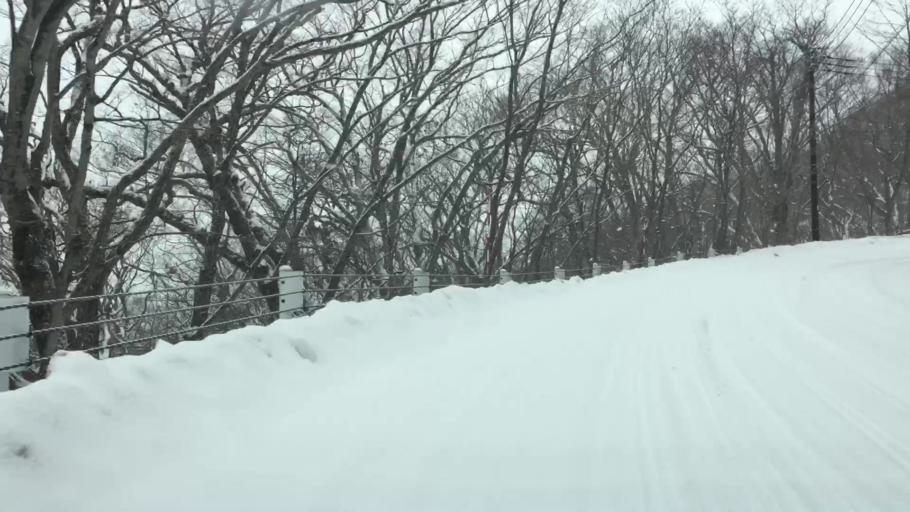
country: JP
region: Tochigi
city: Imaichi
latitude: 36.9064
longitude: 139.7412
